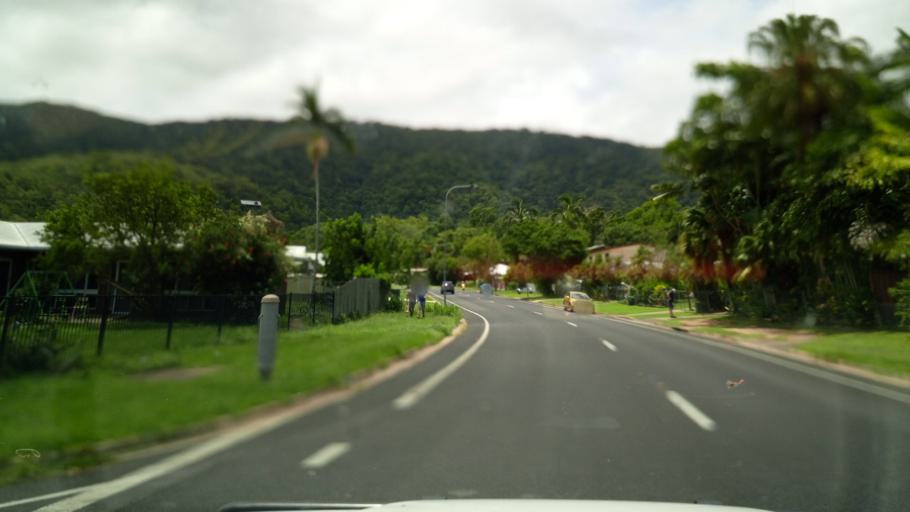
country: AU
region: Queensland
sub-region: Cairns
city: Yorkeys Knob
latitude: -16.8334
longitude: 145.6895
